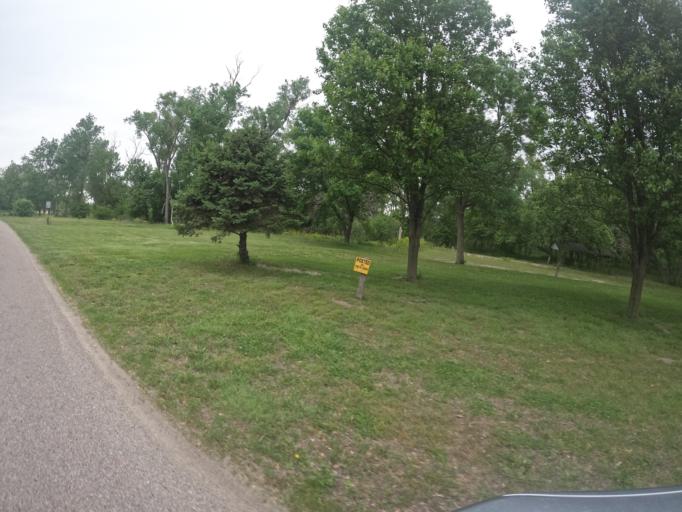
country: US
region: Nebraska
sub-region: Sarpy County
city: Offutt Air Force Base
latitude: 41.0562
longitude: -95.9538
